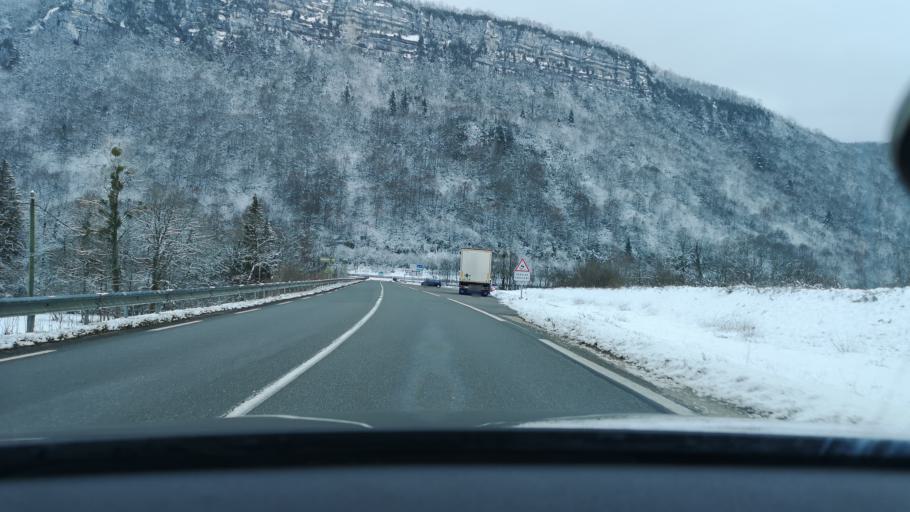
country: FR
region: Rhone-Alpes
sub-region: Departement de l'Ain
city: Dortan
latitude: 46.3645
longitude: 5.7054
